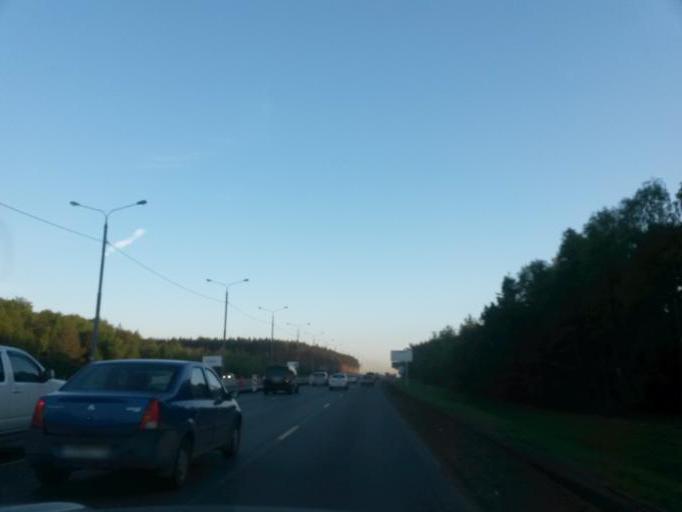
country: RU
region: Moskovskaya
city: Klimovsk
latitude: 55.3654
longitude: 37.6017
